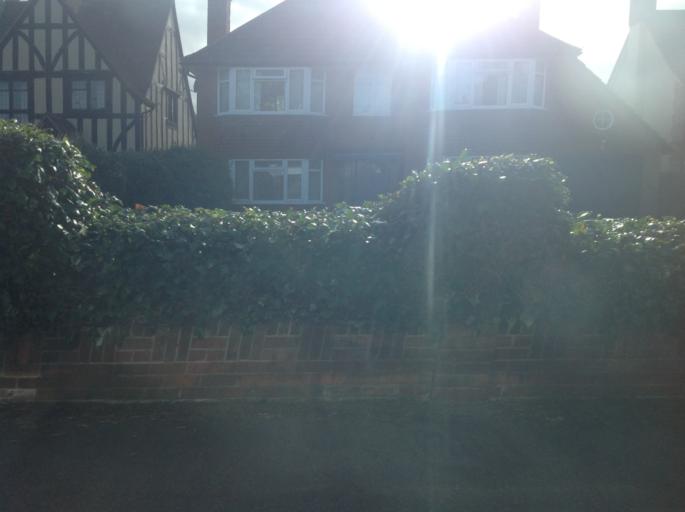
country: GB
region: England
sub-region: Suffolk
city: Felixstowe
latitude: 51.9699
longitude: 1.3520
